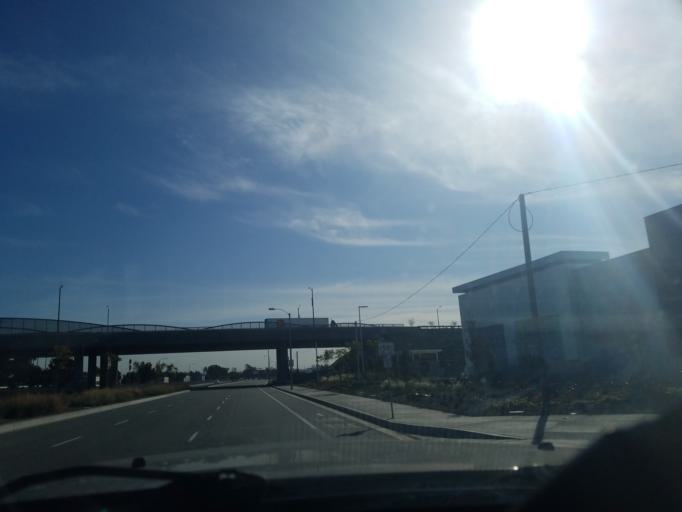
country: US
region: California
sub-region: Orange County
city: Tustin
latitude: 33.7139
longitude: -117.8151
